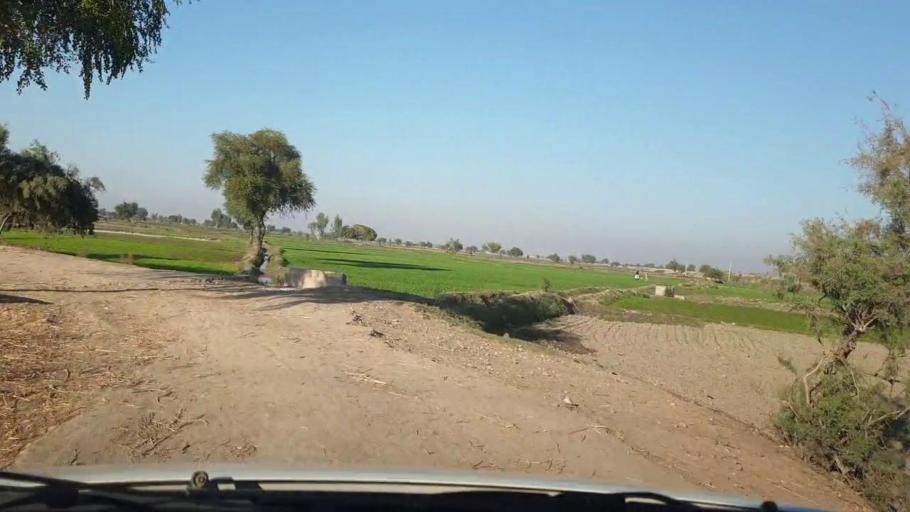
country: PK
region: Sindh
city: Khairpur Nathan Shah
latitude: 27.0386
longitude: 67.7115
